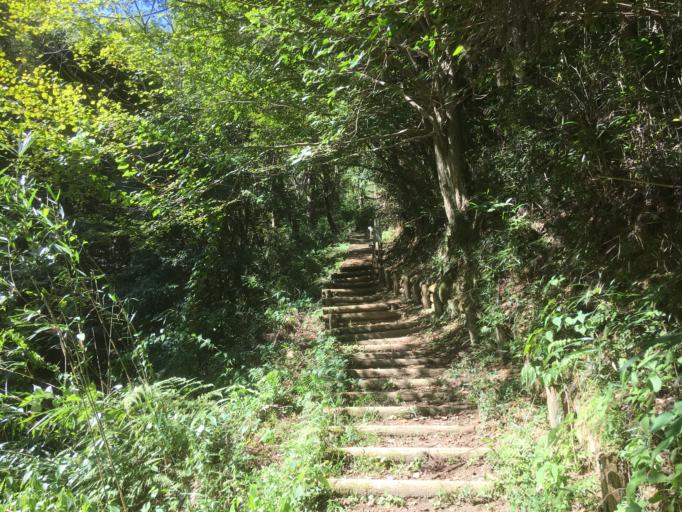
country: JP
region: Nara
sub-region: Ikoma-shi
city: Ikoma
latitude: 34.7266
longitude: 135.6773
